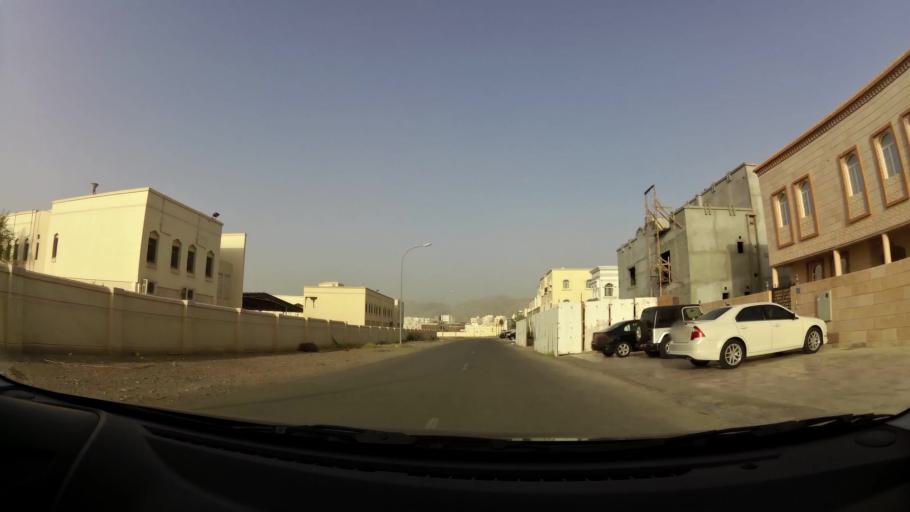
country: OM
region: Muhafazat Masqat
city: Bawshar
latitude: 23.5346
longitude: 58.3485
